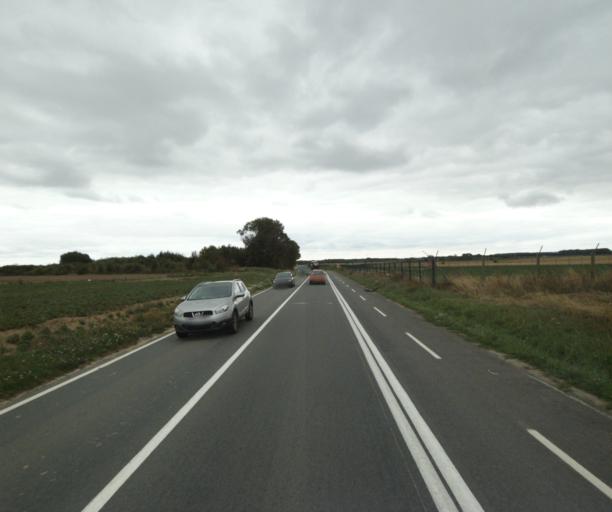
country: FR
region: Nord-Pas-de-Calais
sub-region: Departement du Nord
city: Lesquin
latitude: 50.5726
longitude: 3.1207
